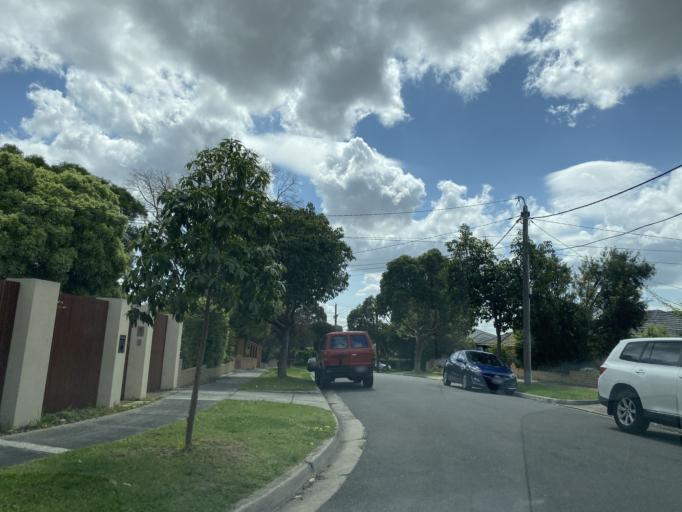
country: AU
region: Victoria
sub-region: Monash
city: Ashwood
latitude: -37.8584
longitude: 145.1064
